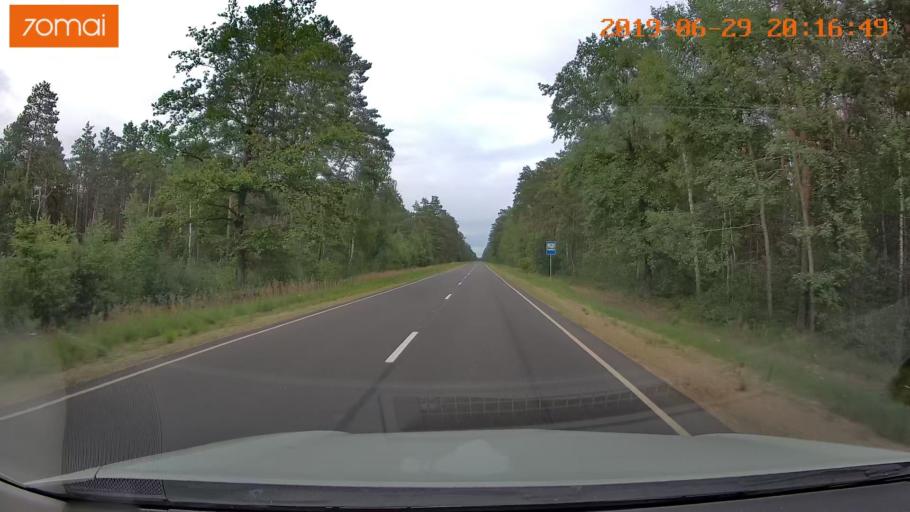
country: BY
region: Brest
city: Asnyezhytsy
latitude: 52.3838
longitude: 26.2039
